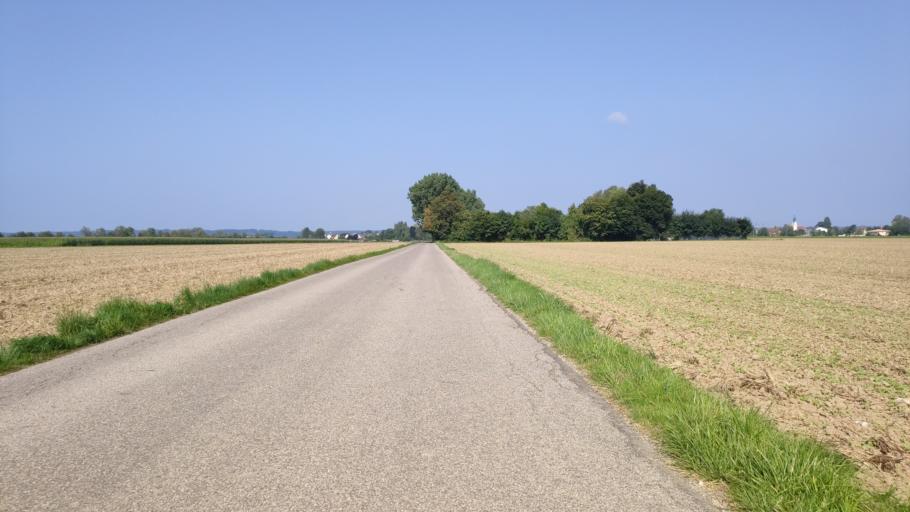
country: DE
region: Bavaria
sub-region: Swabia
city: Bobingen
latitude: 48.2579
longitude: 10.8413
